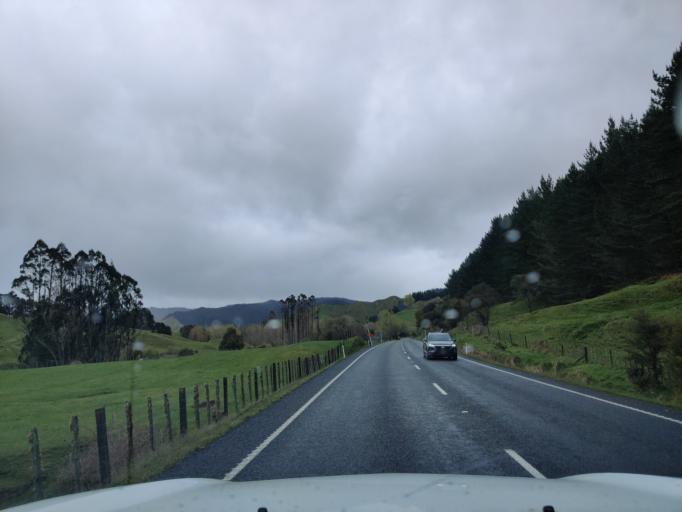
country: NZ
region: Waikato
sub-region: Otorohanga District
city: Otorohanga
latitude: -38.6661
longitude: 175.2051
